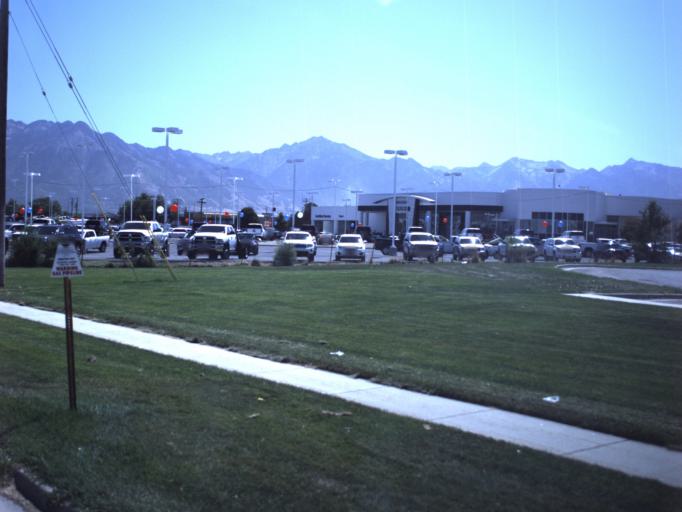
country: US
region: Utah
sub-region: Salt Lake County
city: Centerfield
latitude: 40.6993
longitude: -111.9137
